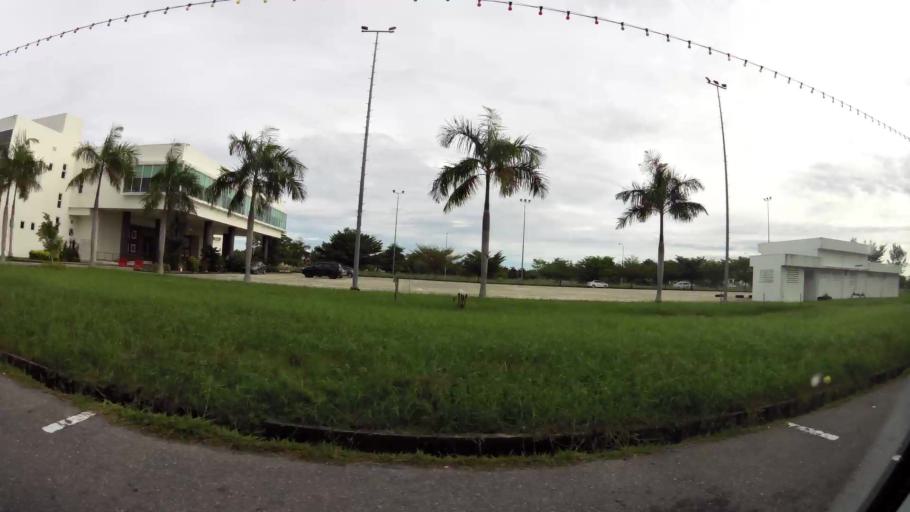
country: BN
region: Belait
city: Seria
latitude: 4.6144
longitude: 114.3288
